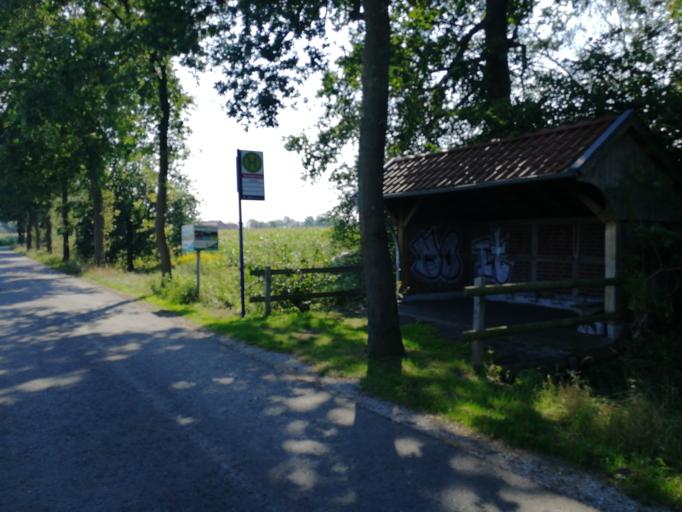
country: DE
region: North Rhine-Westphalia
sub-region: Regierungsbezirk Munster
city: Sassenberg
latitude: 51.9489
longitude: 8.0356
